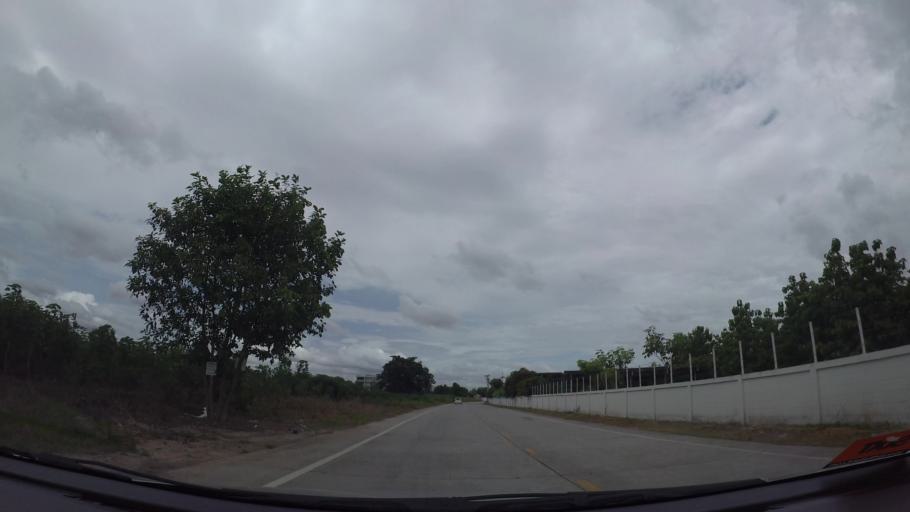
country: TH
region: Chon Buri
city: Si Racha
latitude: 13.1650
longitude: 100.9863
